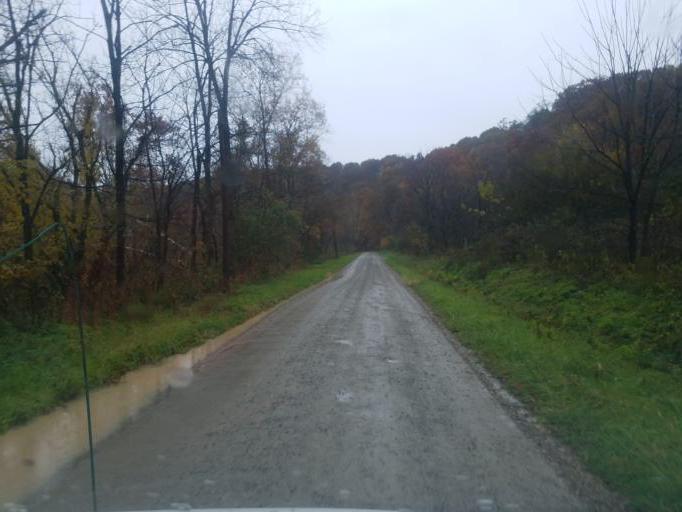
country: US
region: Ohio
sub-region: Washington County
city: Beverly
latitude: 39.4783
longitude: -81.7373
